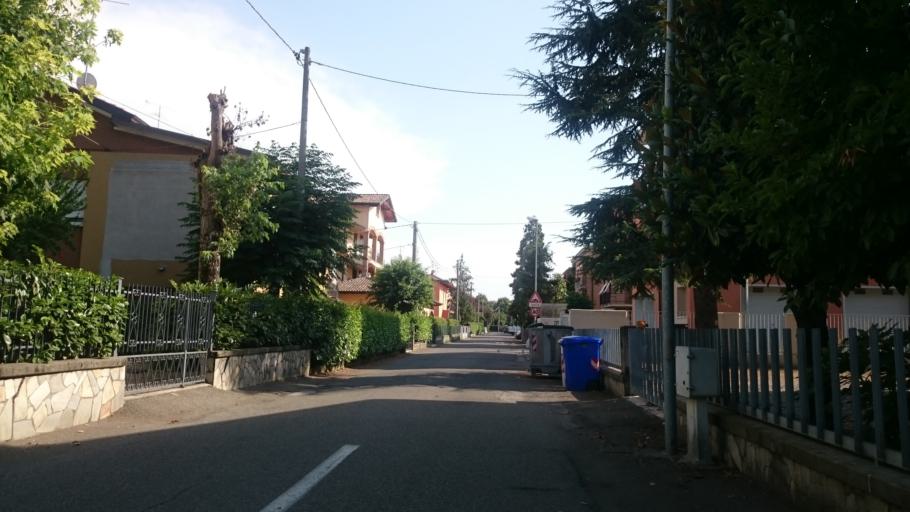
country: IT
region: Emilia-Romagna
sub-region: Provincia di Reggio Emilia
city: Rubiera
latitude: 44.6499
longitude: 10.7791
